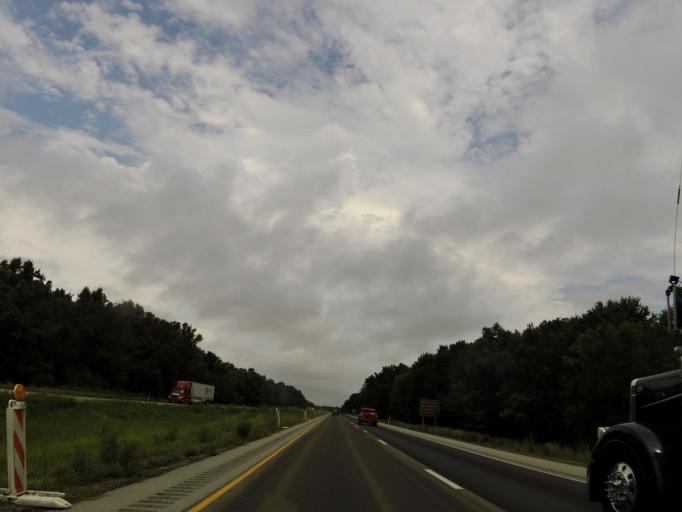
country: US
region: Illinois
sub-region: Franklin County
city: Benton
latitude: 38.0541
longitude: -88.9244
